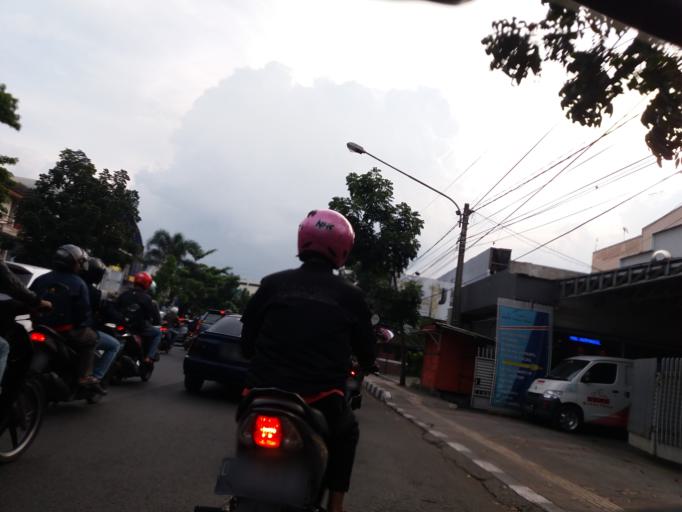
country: ID
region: West Java
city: Bandung
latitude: -6.9145
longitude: 107.6372
